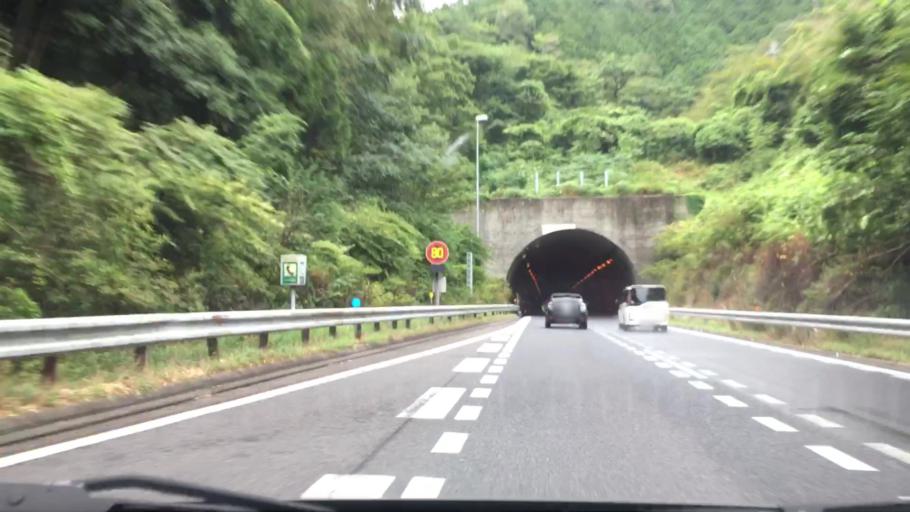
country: JP
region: Okayama
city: Tsuyama
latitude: 35.0148
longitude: 134.2679
